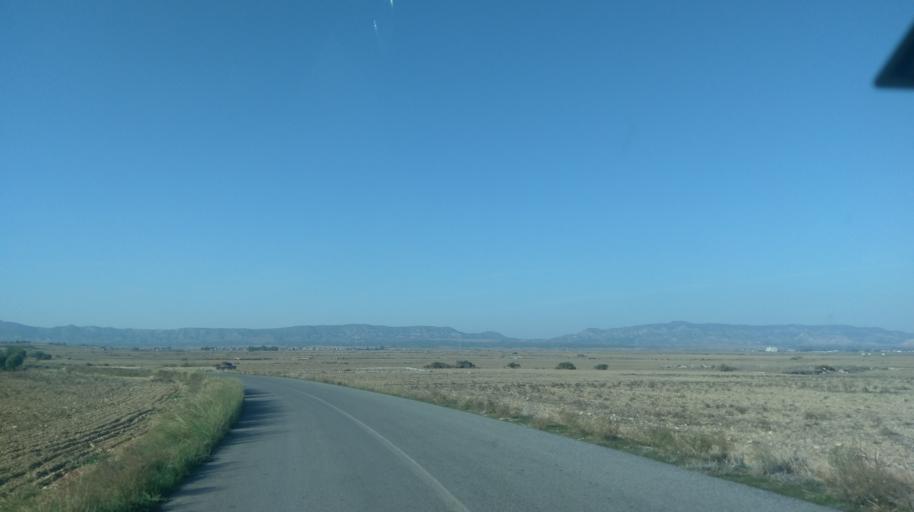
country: CY
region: Ammochostos
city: Lefkonoiko
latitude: 35.2223
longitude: 33.6969
